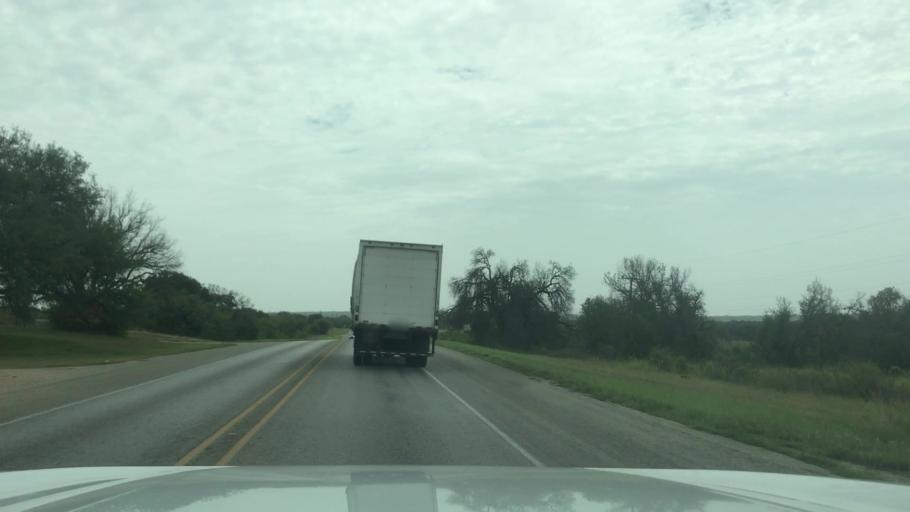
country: US
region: Texas
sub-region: Comanche County
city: De Leon
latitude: 32.1003
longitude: -98.4733
